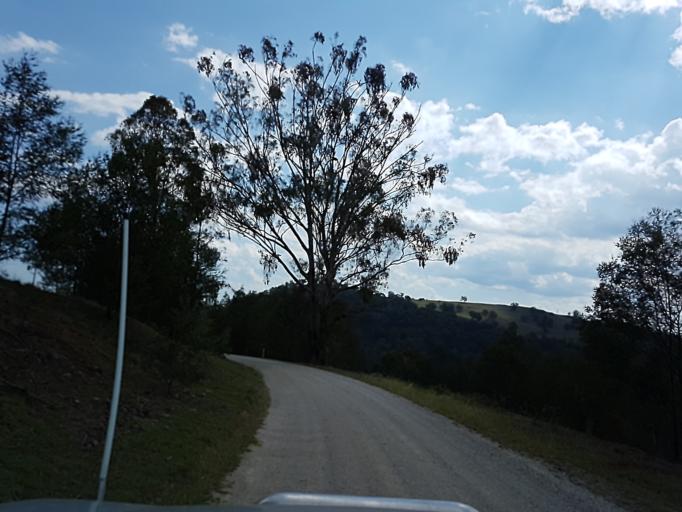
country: AU
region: Victoria
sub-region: East Gippsland
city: Lakes Entrance
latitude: -37.4811
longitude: 148.2394
